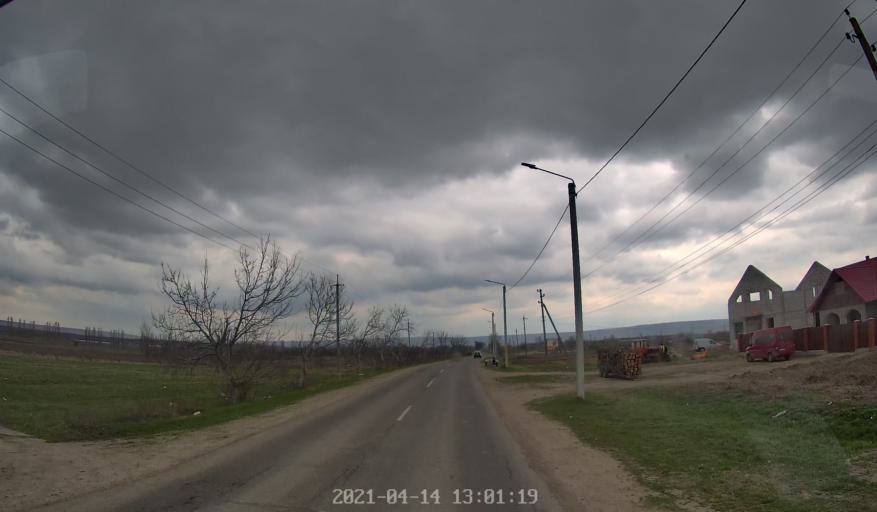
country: MD
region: Chisinau
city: Vadul lui Voda
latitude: 47.1327
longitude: 29.1171
